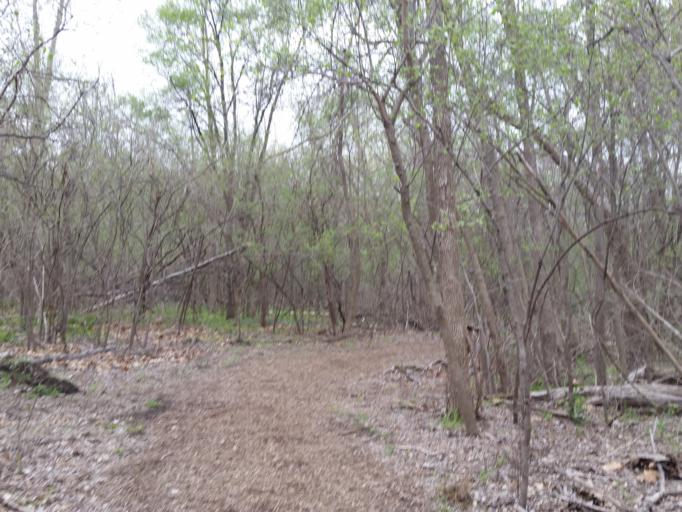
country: US
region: Nebraska
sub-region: Sarpy County
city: Bellevue
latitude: 41.1488
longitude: -95.8850
